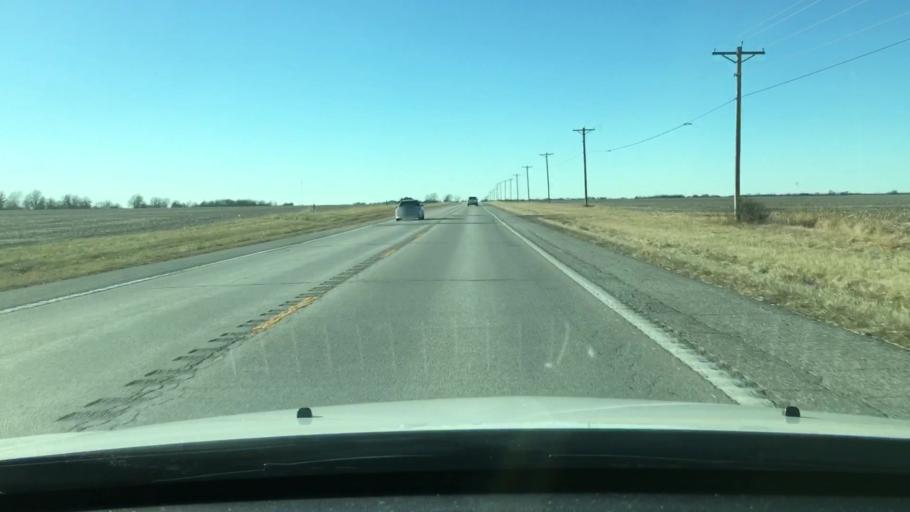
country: US
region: Missouri
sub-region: Audrain County
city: Vandalia
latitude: 39.3460
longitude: -91.3684
